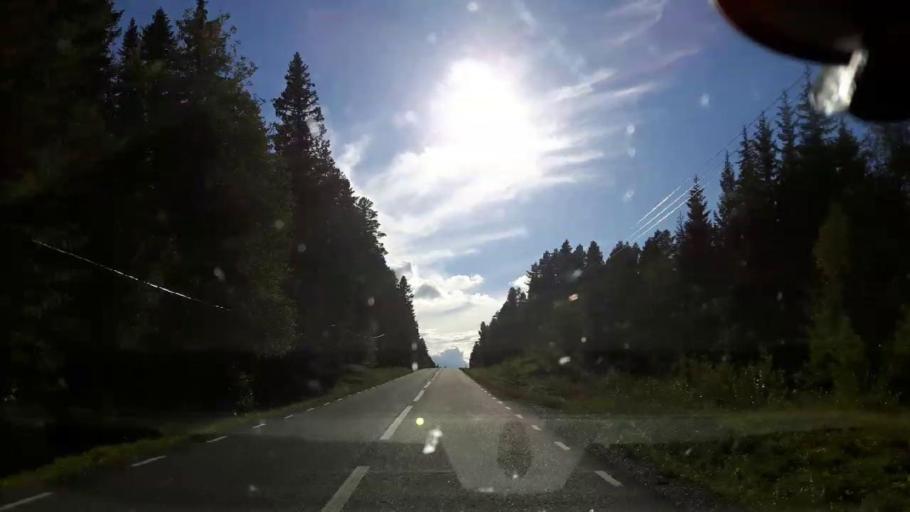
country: SE
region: Jaemtland
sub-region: Stroemsunds Kommun
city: Stroemsund
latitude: 63.5671
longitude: 15.6086
